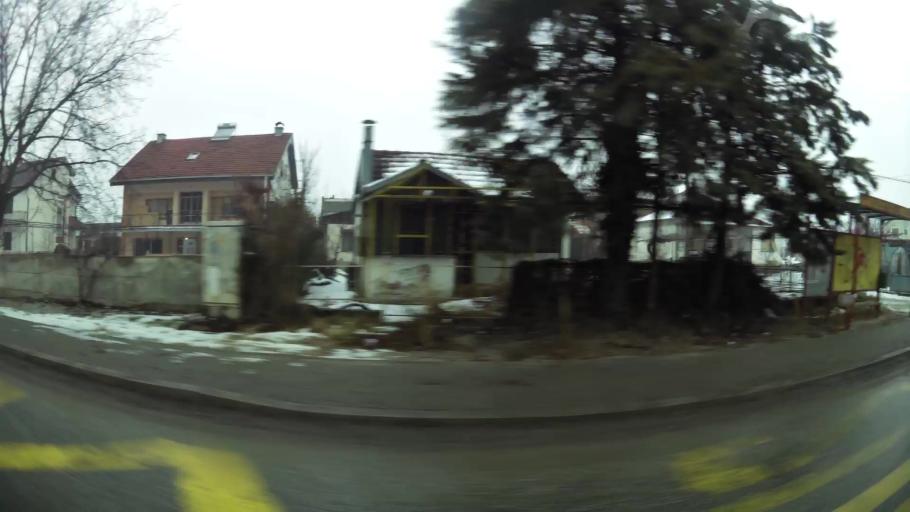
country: MK
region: Petrovec
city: Petrovec
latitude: 41.9331
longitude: 21.6226
